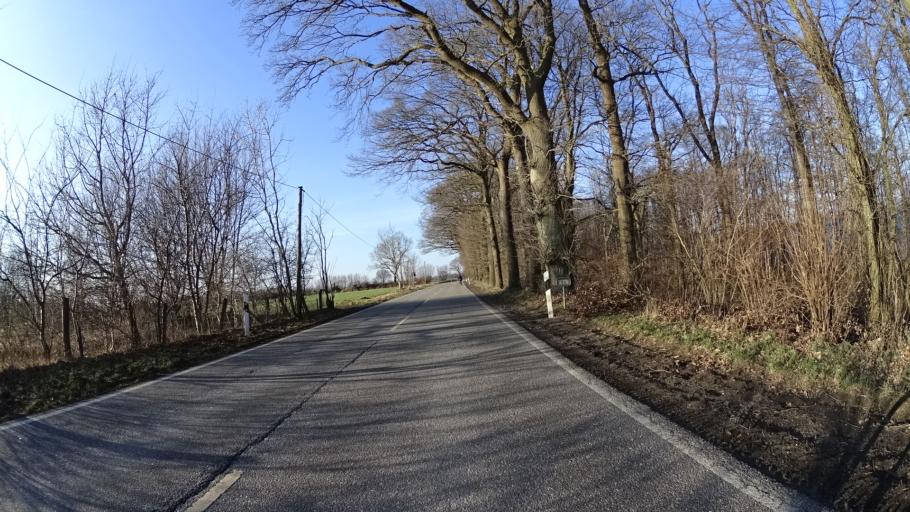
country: DE
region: Schleswig-Holstein
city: Martensrade
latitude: 54.3071
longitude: 10.3812
